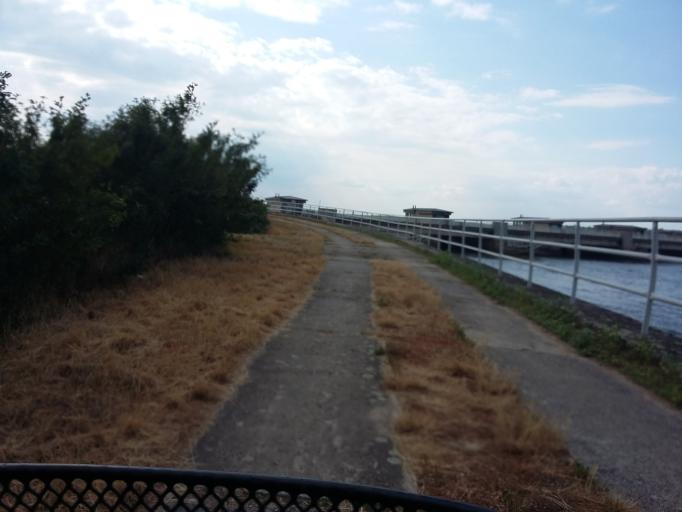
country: CZ
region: South Moravian
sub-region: Okres Breclav
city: Dolni Dunajovice
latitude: 48.8925
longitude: 16.6452
